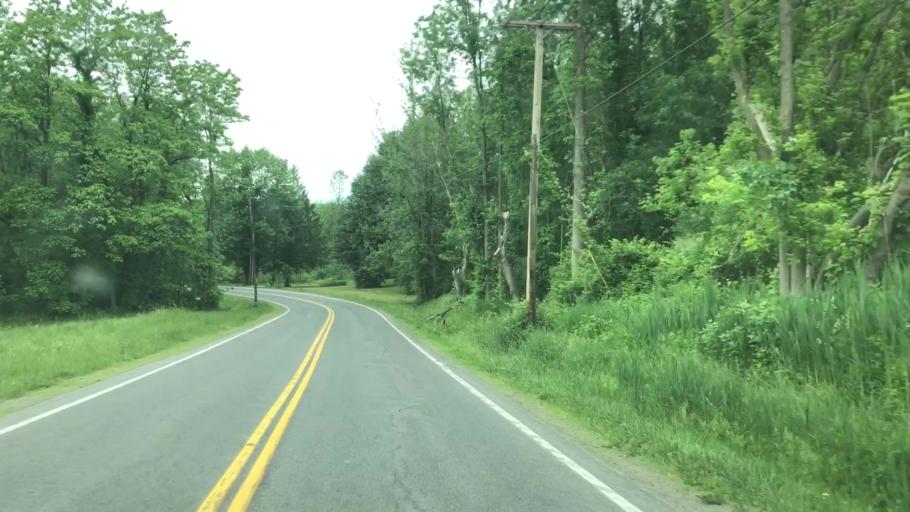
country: US
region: New York
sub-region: Wayne County
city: Macedon
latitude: 43.1173
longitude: -77.2883
